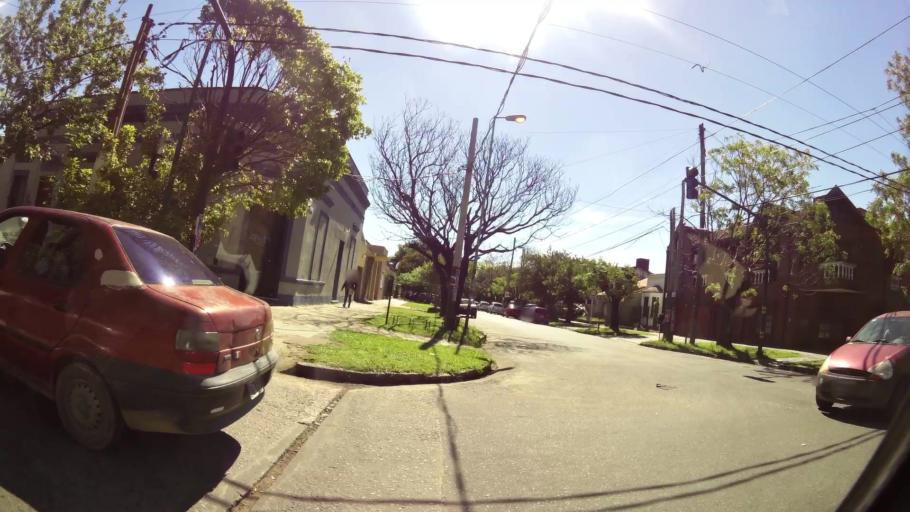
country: AR
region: Buenos Aires
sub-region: Partido de Lomas de Zamora
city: Lomas de Zamora
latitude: -34.7585
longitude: -58.4083
